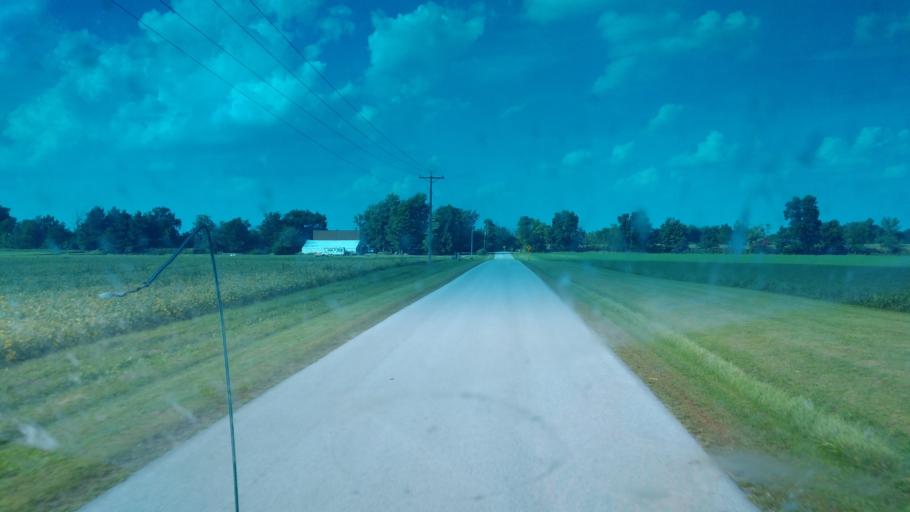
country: US
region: Ohio
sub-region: Hancock County
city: Arlington
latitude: 40.8776
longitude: -83.5709
